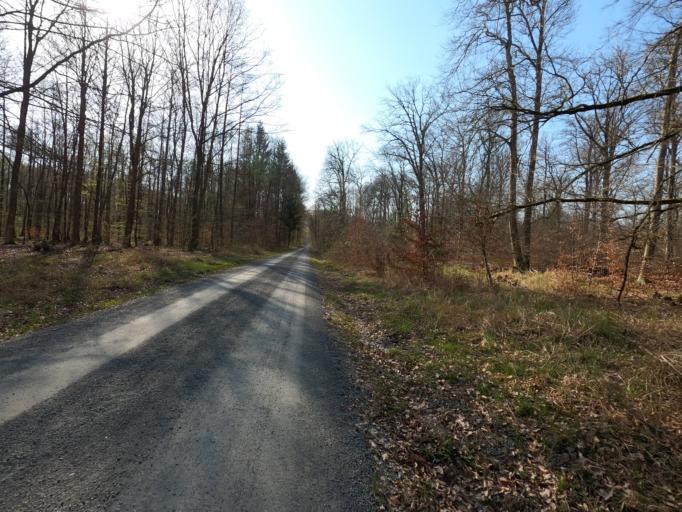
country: DE
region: Hesse
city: Morfelden-Walldorf
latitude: 49.9538
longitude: 8.5534
